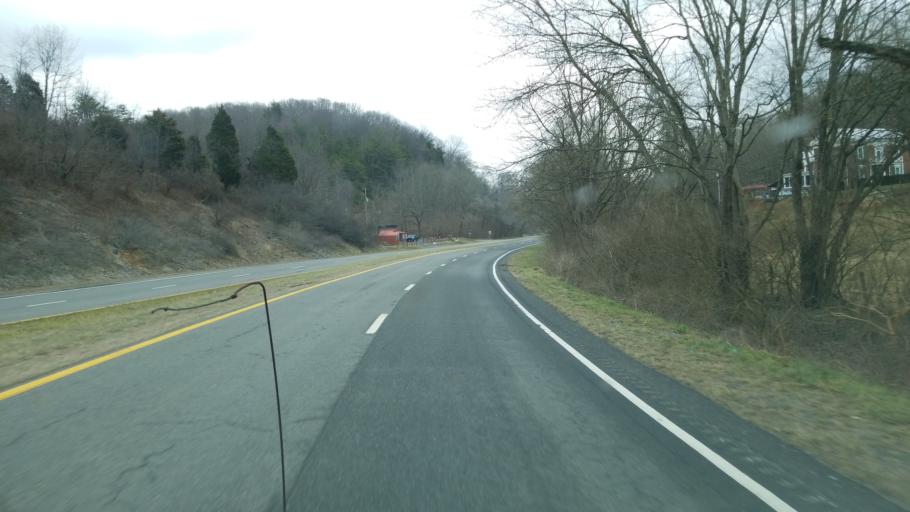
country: US
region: Virginia
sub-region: Giles County
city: Pearisburg
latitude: 37.2739
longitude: -80.7376
